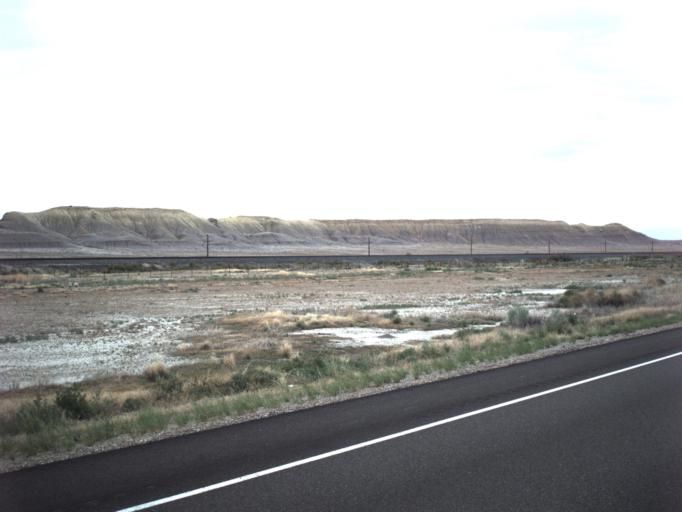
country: US
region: Utah
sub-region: Carbon County
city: East Carbon City
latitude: 39.0122
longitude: -110.2841
